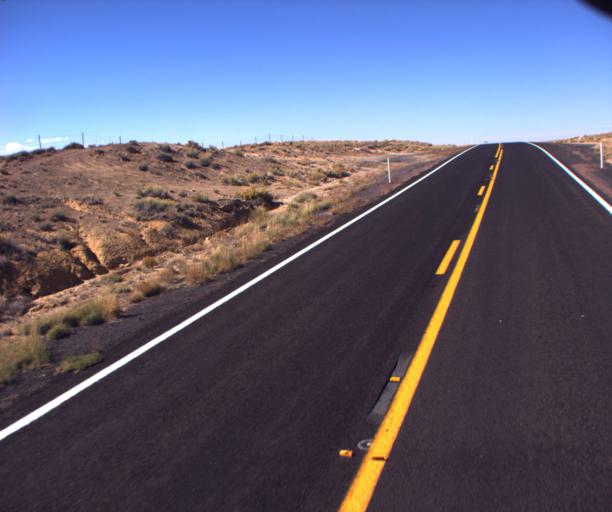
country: US
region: Arizona
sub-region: Coconino County
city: Tuba City
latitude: 35.9581
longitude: -110.9336
